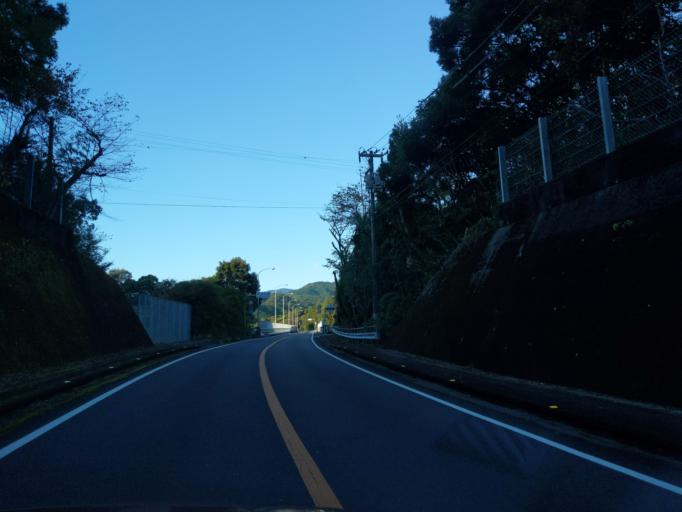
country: JP
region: Kochi
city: Muroto-misakicho
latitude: 33.5467
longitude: 134.3032
